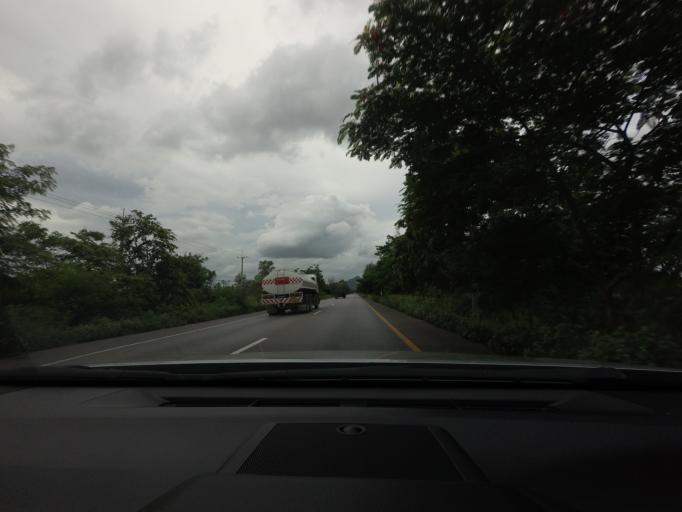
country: TH
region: Phetchaburi
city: Cha-am
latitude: 12.7686
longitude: 99.9351
